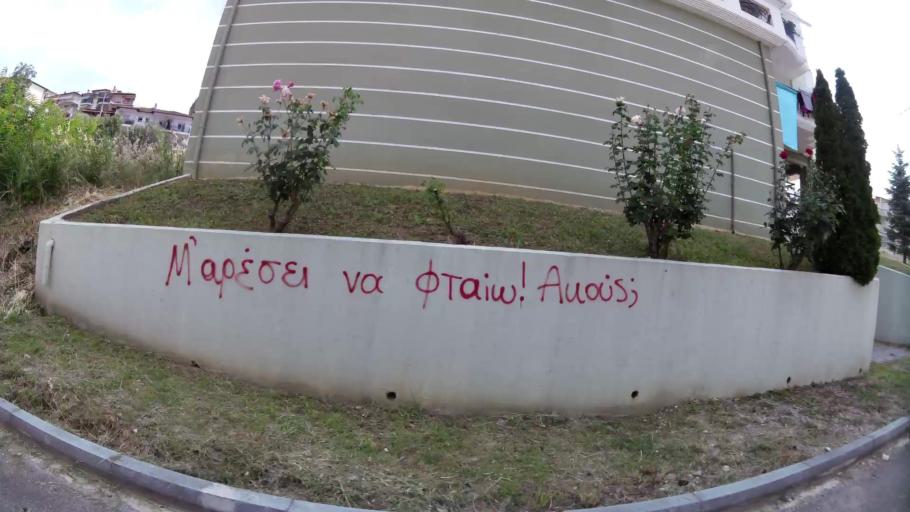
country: GR
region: Central Macedonia
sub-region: Nomos Imathias
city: Veroia
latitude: 40.5155
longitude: 22.2082
